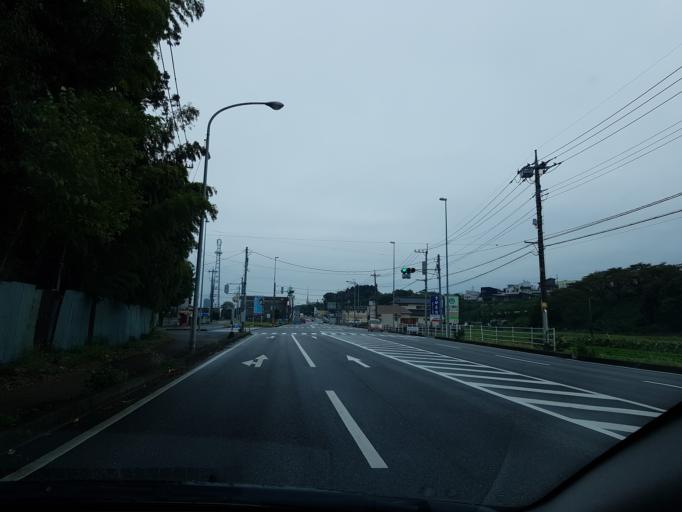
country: JP
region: Tochigi
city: Utsunomiya-shi
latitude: 36.5873
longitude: 139.8932
